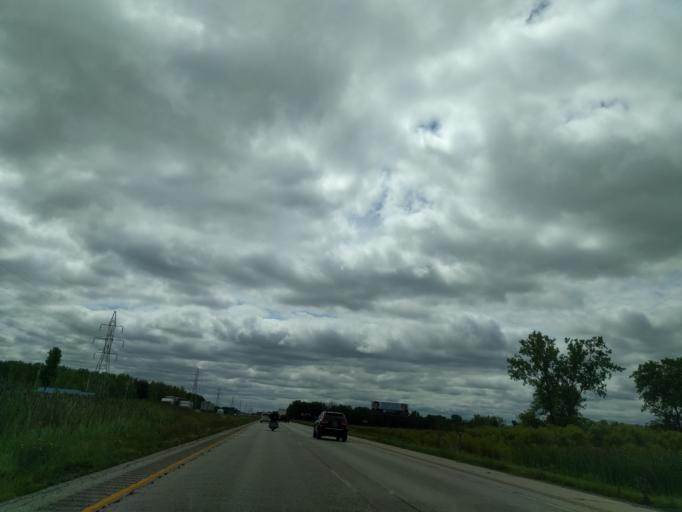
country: US
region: Wisconsin
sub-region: Brown County
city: Suamico
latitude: 44.6197
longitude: -88.0501
